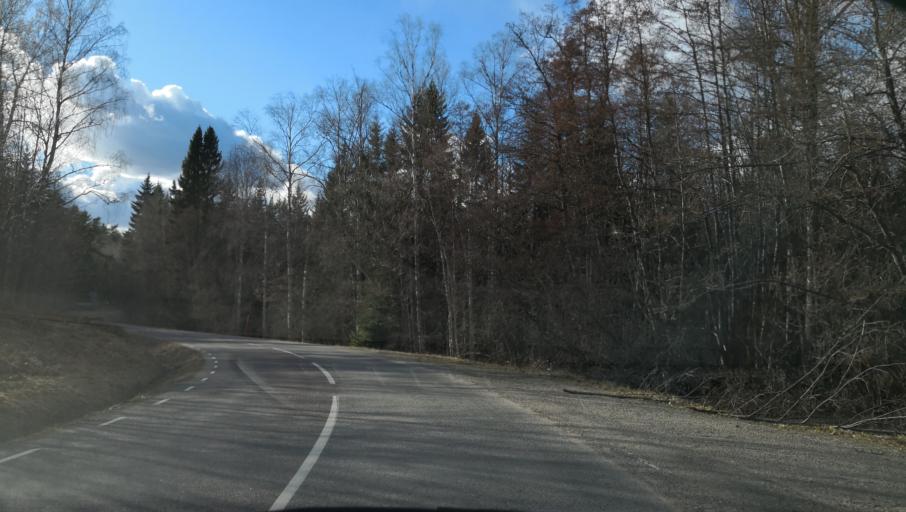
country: SE
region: Stockholm
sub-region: Varmdo Kommun
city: Hemmesta
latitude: 59.2872
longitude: 18.4768
